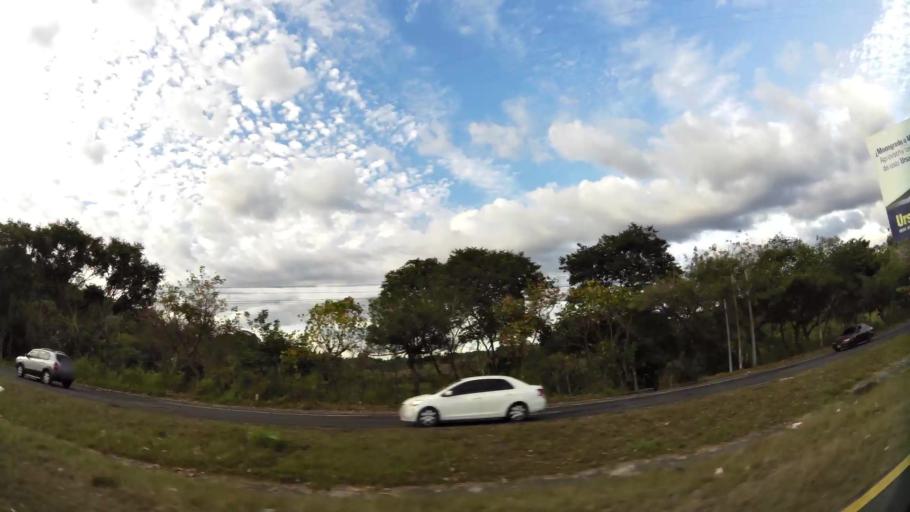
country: SV
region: San Vicente
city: San Sebastian
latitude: 13.7265
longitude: -88.8648
